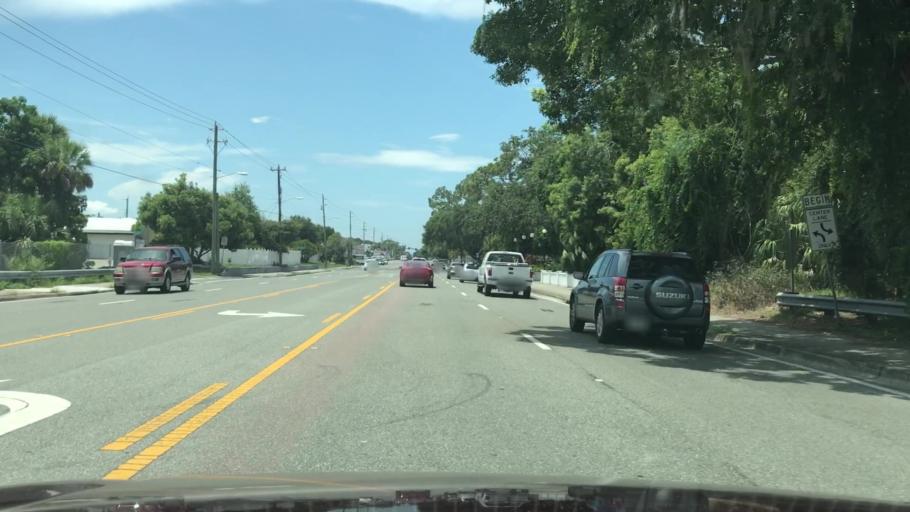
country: US
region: Florida
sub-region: Sarasota County
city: Southgate
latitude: 27.3037
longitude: -82.5142
